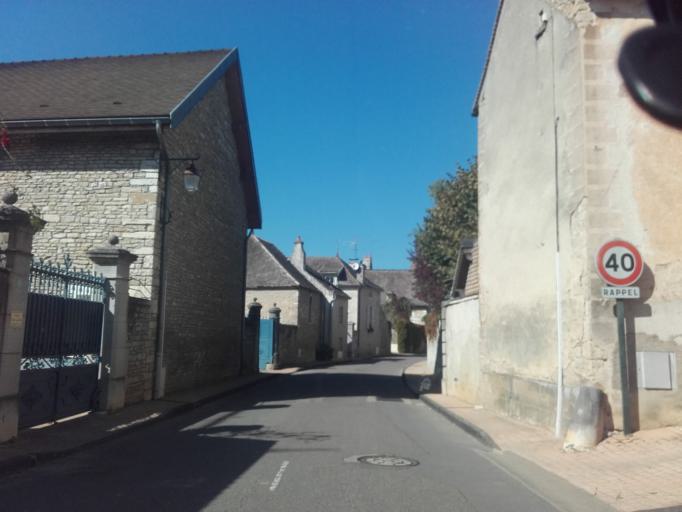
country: FR
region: Bourgogne
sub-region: Departement de la Cote-d'Or
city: Meursault
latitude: 46.9823
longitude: 4.7669
